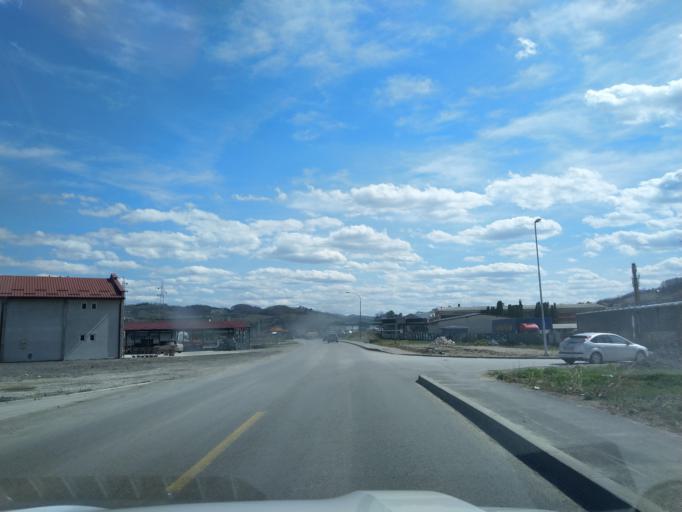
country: RS
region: Central Serbia
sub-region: Zlatiborski Okrug
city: Arilje
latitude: 43.7590
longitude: 20.0978
